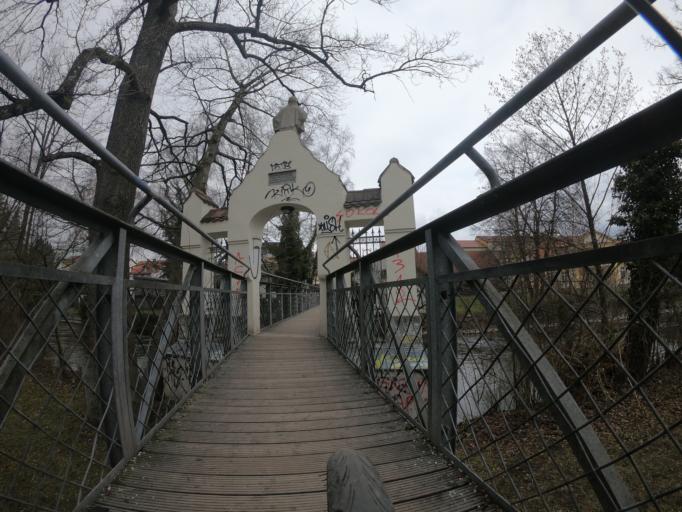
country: DE
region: Bavaria
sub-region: Upper Bavaria
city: Fuerstenfeldbruck
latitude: 48.1759
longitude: 11.2534
